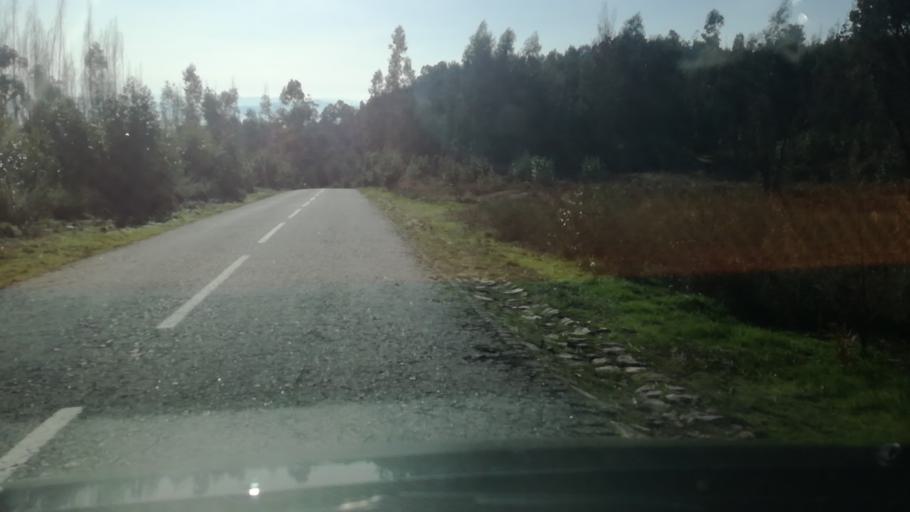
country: PT
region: Braga
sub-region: Braga
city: Braga
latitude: 41.5343
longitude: -8.3566
